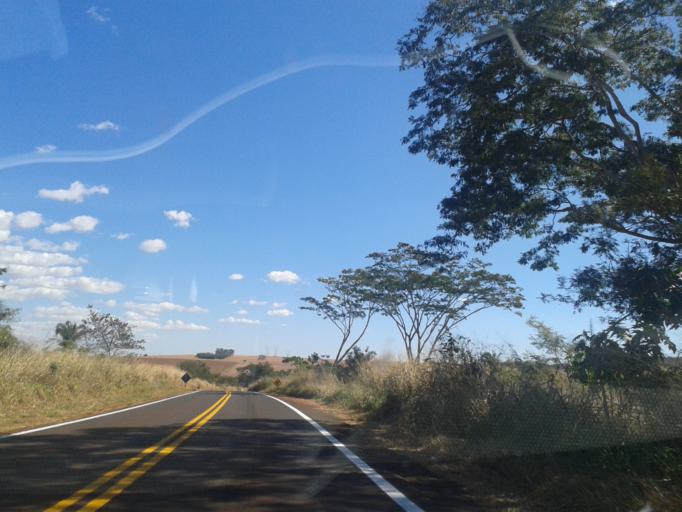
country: BR
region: Minas Gerais
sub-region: Capinopolis
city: Capinopolis
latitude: -18.6908
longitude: -49.4515
